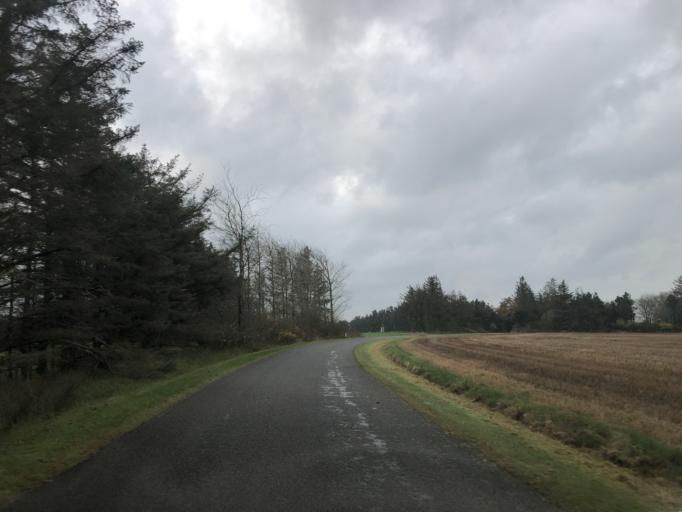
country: DK
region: Central Jutland
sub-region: Holstebro Kommune
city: Ulfborg
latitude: 56.3160
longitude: 8.2201
